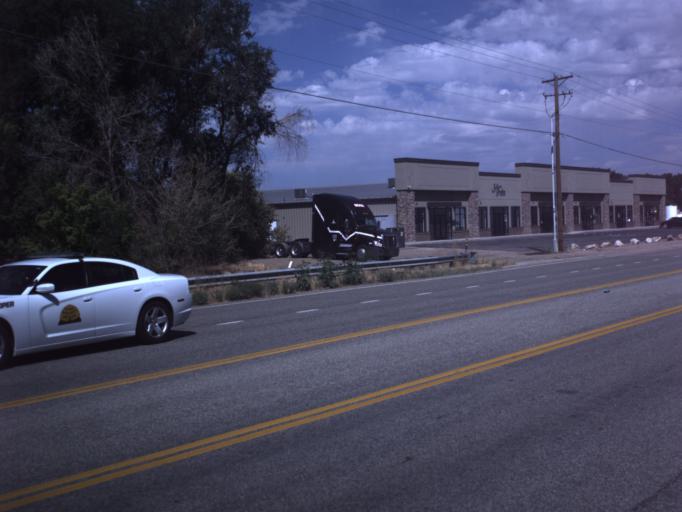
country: US
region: Utah
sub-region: Box Elder County
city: South Willard
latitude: 41.3483
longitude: -112.0341
